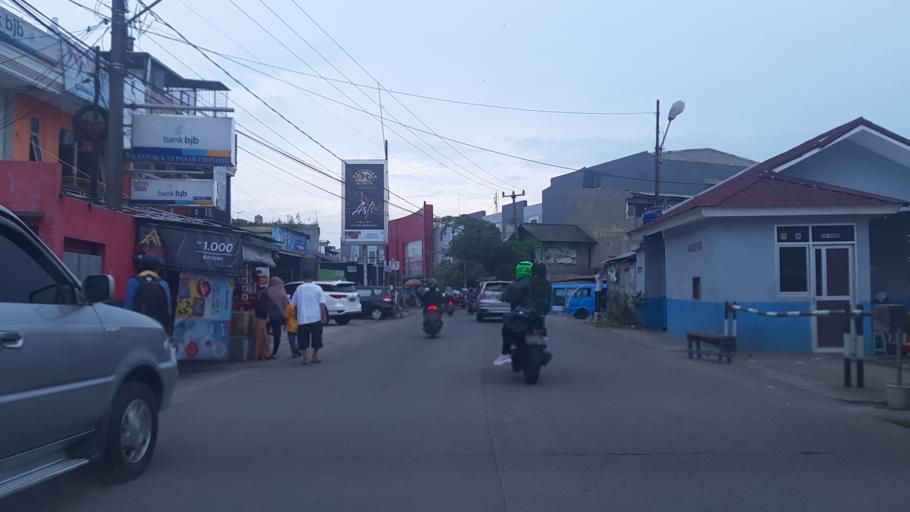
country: ID
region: West Java
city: Cibinong
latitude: -6.4681
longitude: 106.8550
